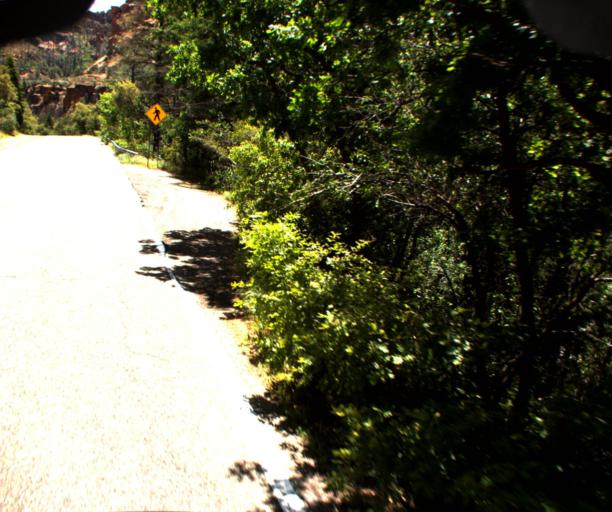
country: US
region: Arizona
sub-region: Coconino County
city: Sedona
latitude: 34.9580
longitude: -111.7540
